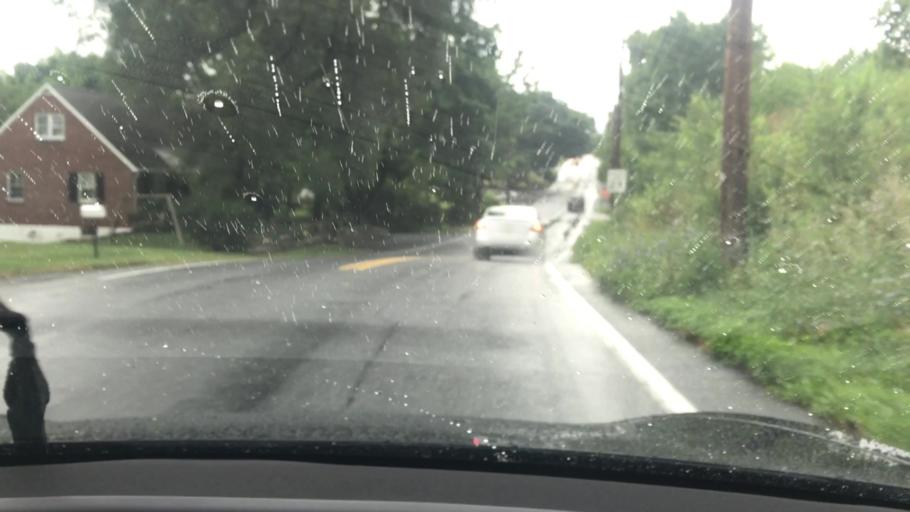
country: US
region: Pennsylvania
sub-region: Dauphin County
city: Paxtonia
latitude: 40.3202
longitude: -76.7989
